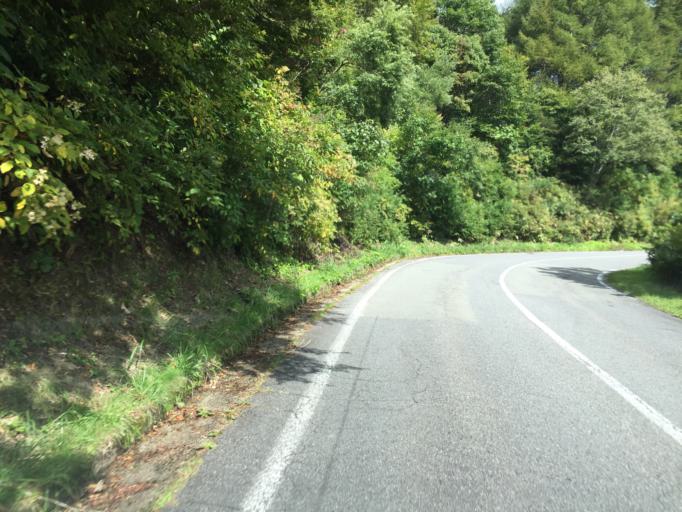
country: JP
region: Fukushima
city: Inawashiro
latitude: 37.6041
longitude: 140.0485
